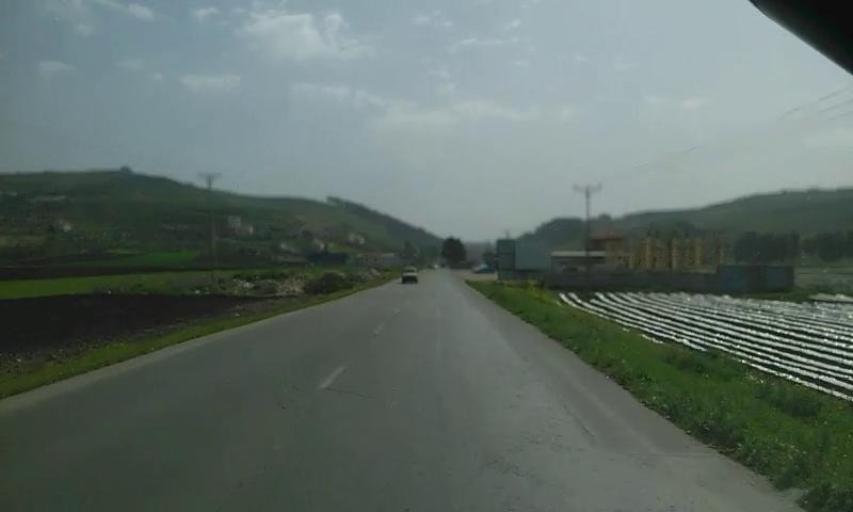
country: PS
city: Bir al Basha
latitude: 32.4126
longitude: 35.2283
